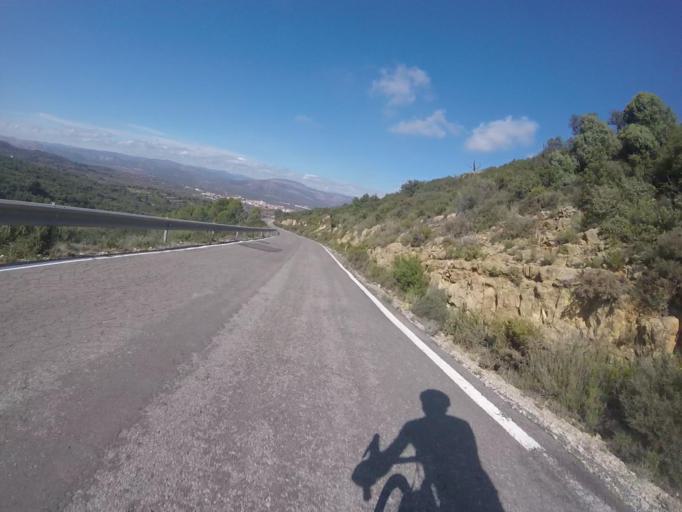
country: ES
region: Valencia
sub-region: Provincia de Castello
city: Albocasser
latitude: 40.3499
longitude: 0.0498
